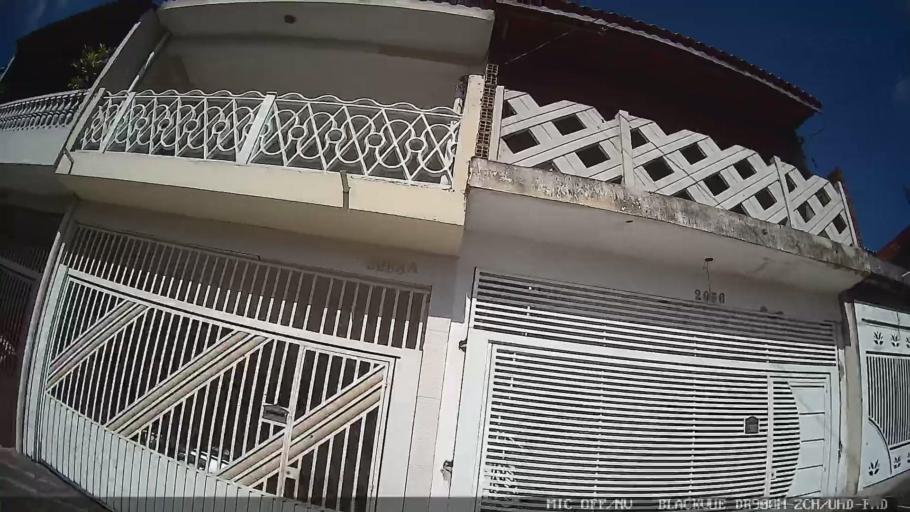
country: BR
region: Sao Paulo
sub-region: Itaquaquecetuba
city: Itaquaquecetuba
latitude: -23.4965
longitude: -46.3406
